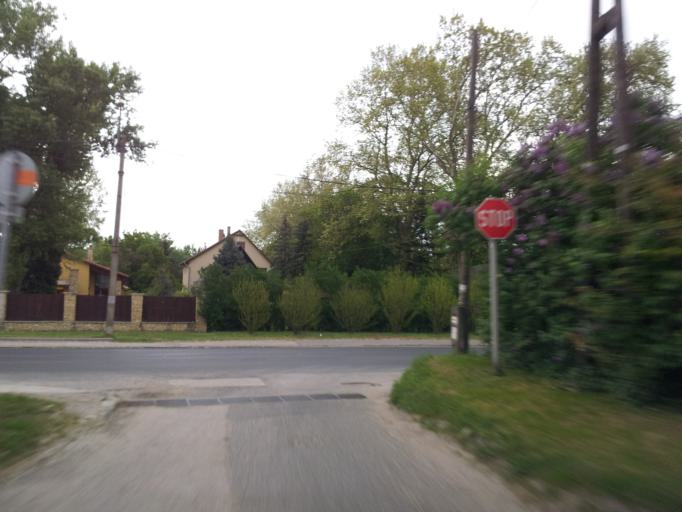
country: HU
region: Pest
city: Tahitotfalu
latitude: 47.7540
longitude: 19.0757
